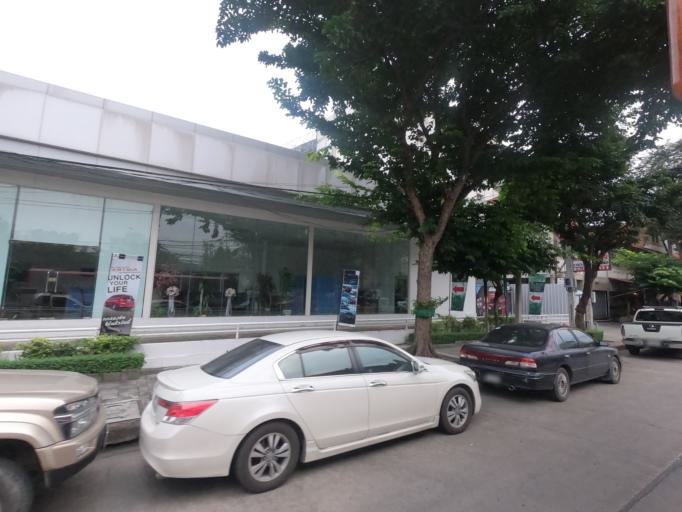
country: TH
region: Bangkok
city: Wang Thonglang
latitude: 13.7887
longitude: 100.6081
